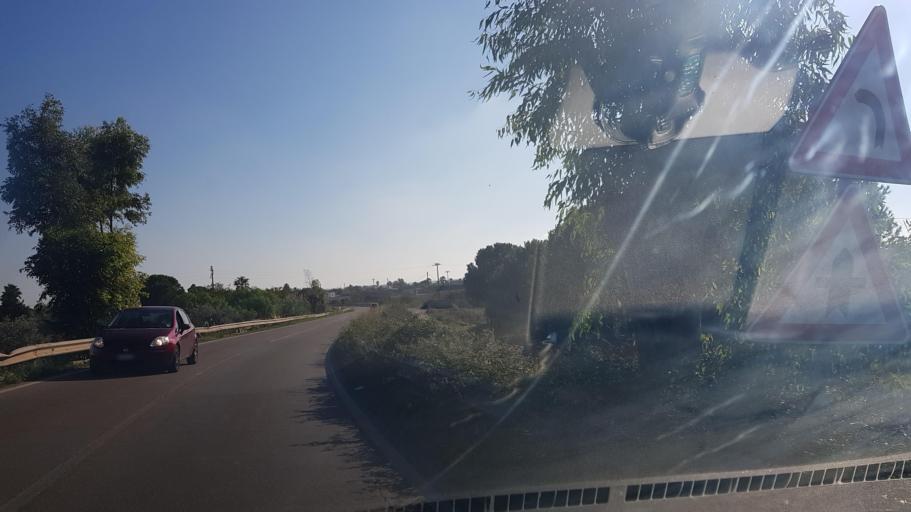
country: IT
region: Apulia
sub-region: Provincia di Lecce
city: Montesano Salentino
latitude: 39.9706
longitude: 18.3283
